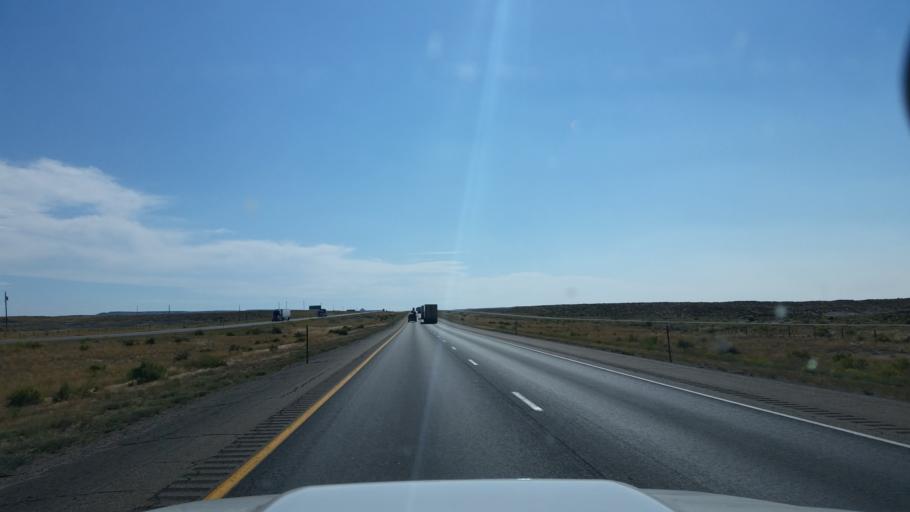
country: US
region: Wyoming
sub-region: Uinta County
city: Lyman
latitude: 41.5299
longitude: -109.9451
